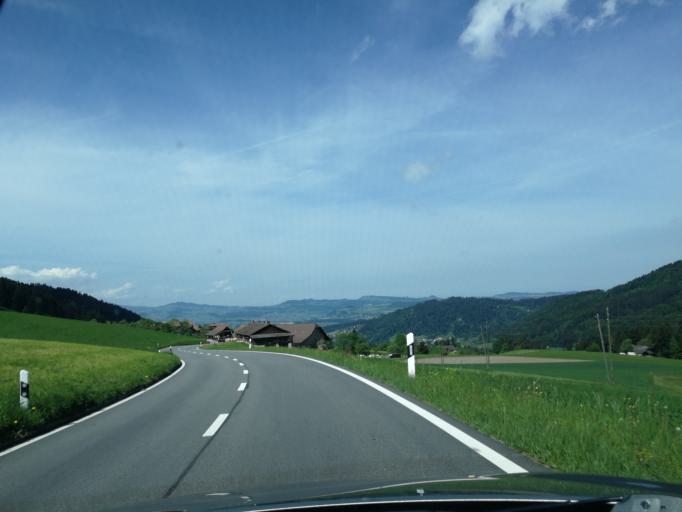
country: CH
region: Bern
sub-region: Bern-Mittelland District
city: Linden
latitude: 46.8391
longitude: 7.6619
